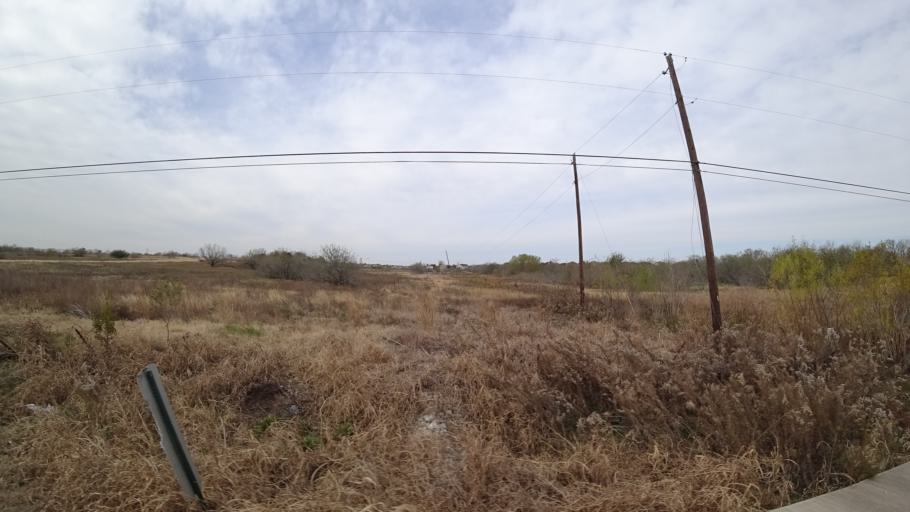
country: US
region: Texas
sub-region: Travis County
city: Garfield
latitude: 30.1522
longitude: -97.6409
